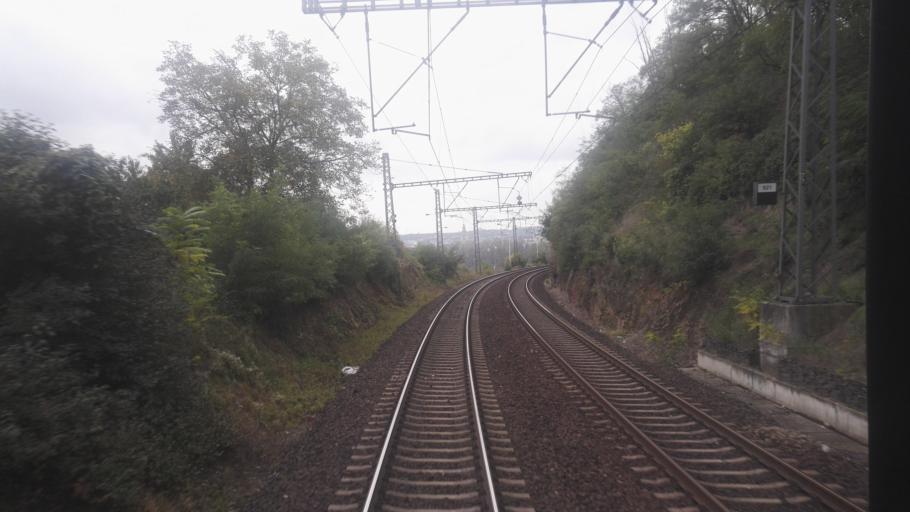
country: CZ
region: Central Bohemia
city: Roztoky
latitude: 50.1266
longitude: 14.3983
